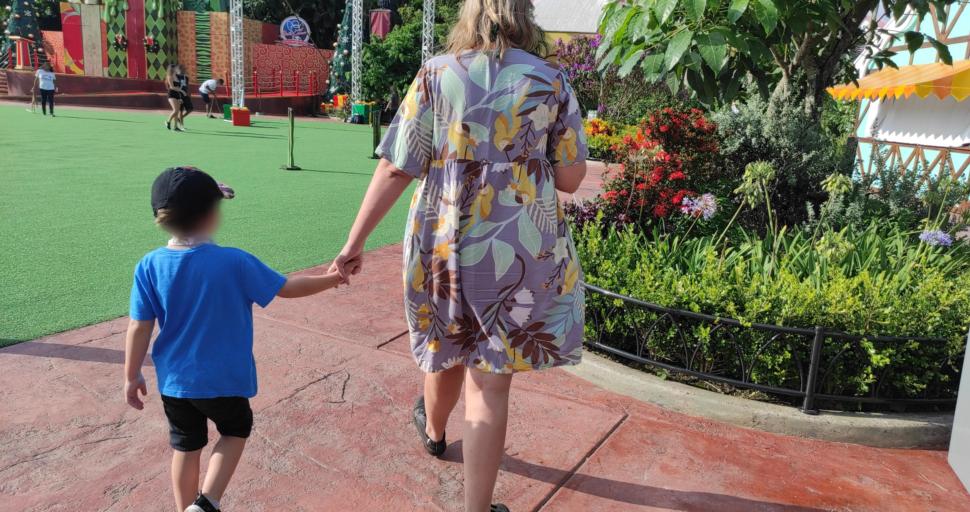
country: BR
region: Santa Catarina
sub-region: Penha
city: Penha
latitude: -26.8009
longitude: -48.6141
